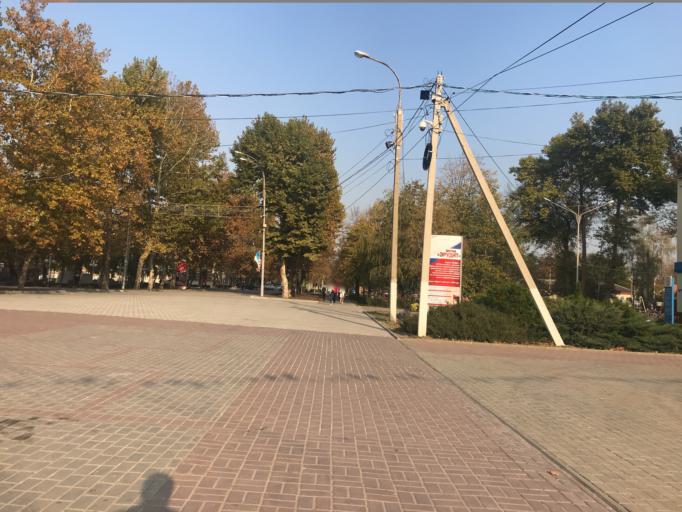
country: RU
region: Krasnodarskiy
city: Slavyansk-na-Kubani
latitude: 45.2602
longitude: 38.1287
